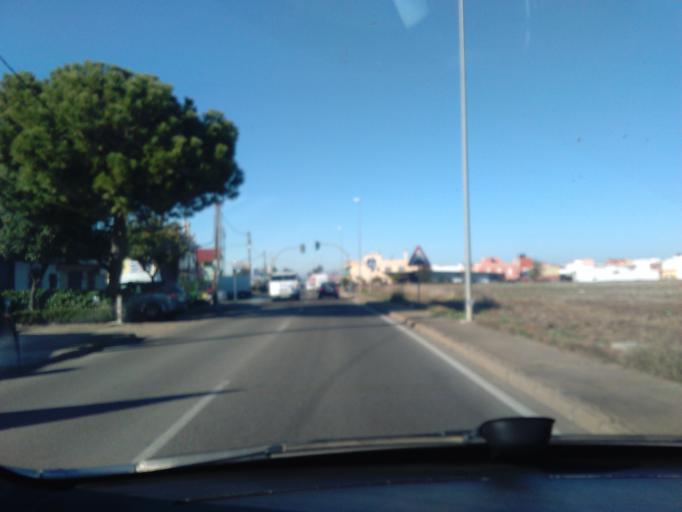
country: ES
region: Andalusia
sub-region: Provincia de Sevilla
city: Sevilla
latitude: 37.4250
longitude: -5.9280
